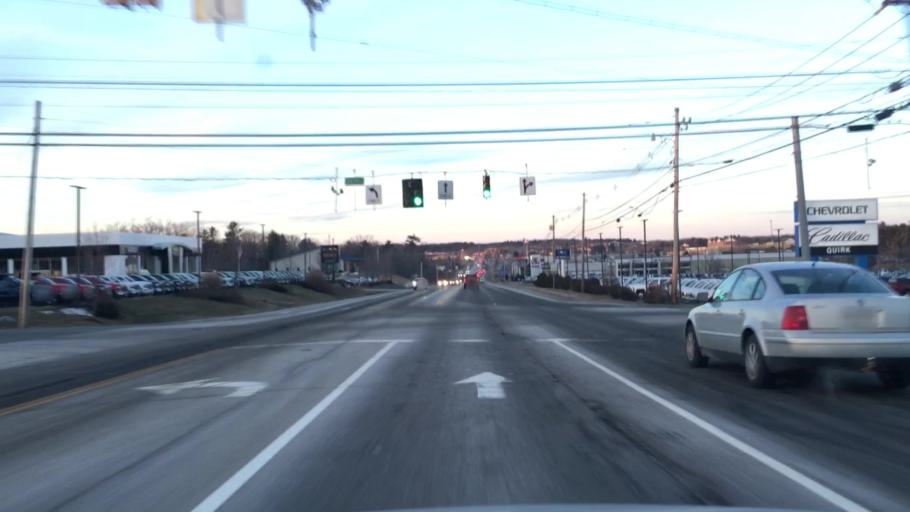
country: US
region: Maine
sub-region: Penobscot County
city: Brewer
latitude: 44.8223
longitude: -68.7395
